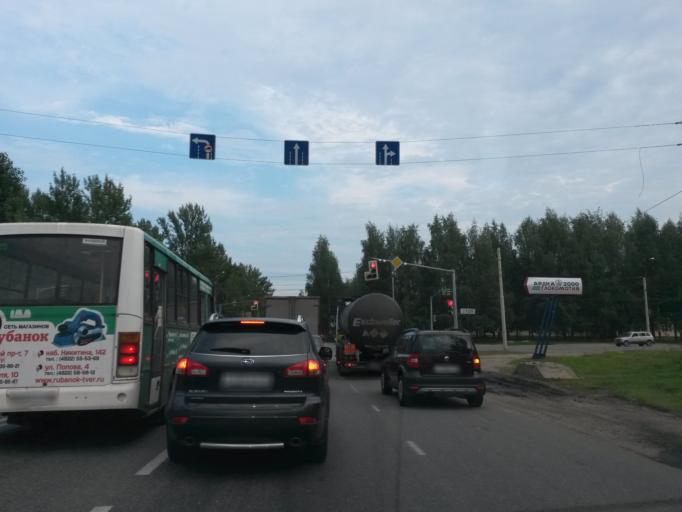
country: RU
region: Jaroslavl
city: Yaroslavl
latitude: 57.5801
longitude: 39.8328
